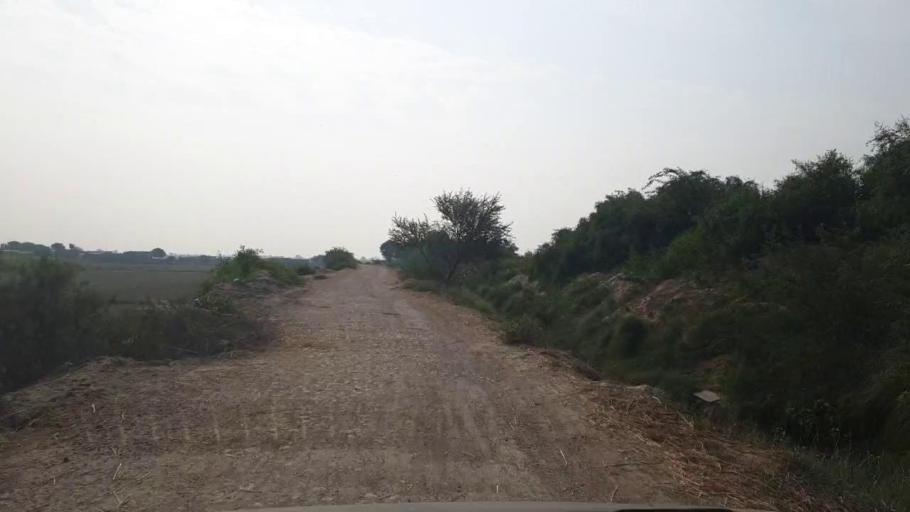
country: PK
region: Sindh
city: Tando Muhammad Khan
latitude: 25.1271
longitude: 68.4911
